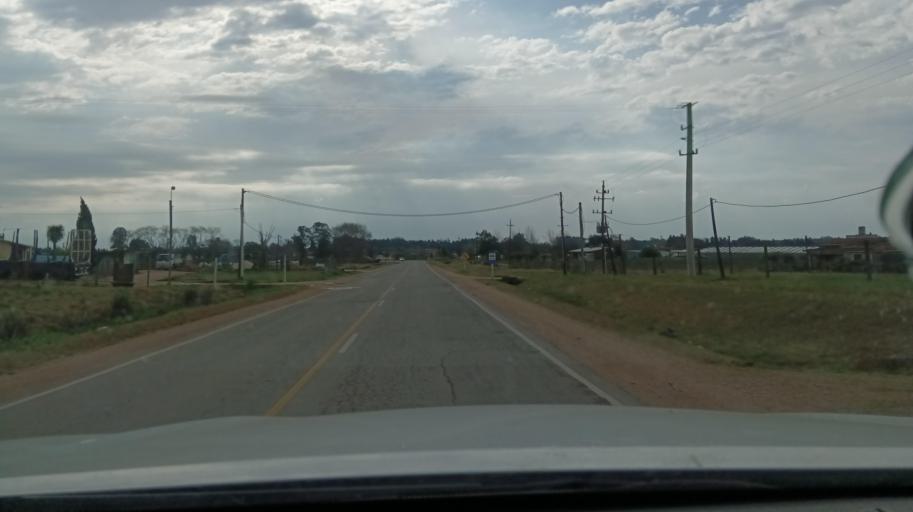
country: UY
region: Canelones
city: Sauce
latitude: -34.6811
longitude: -56.1117
